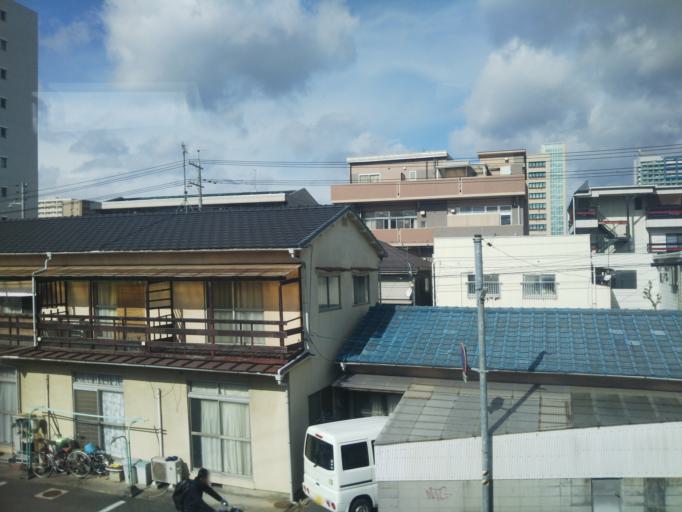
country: JP
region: Okayama
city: Okayama-shi
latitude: 34.6628
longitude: 133.9141
